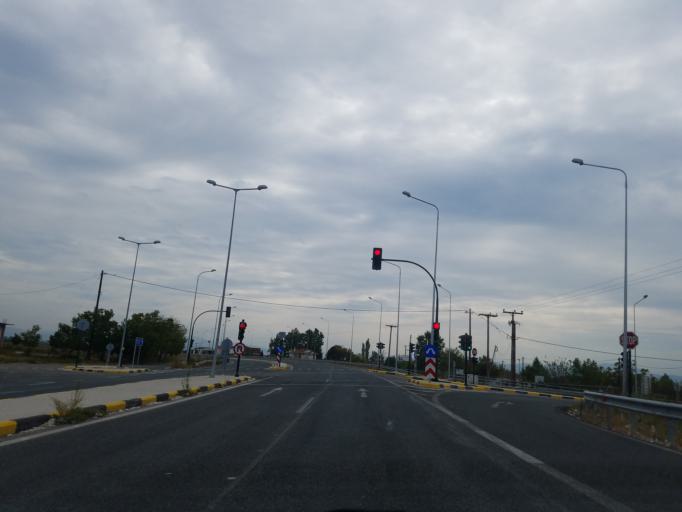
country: GR
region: Thessaly
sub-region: Nomos Kardhitsas
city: Sofades
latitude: 39.3023
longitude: 22.1285
